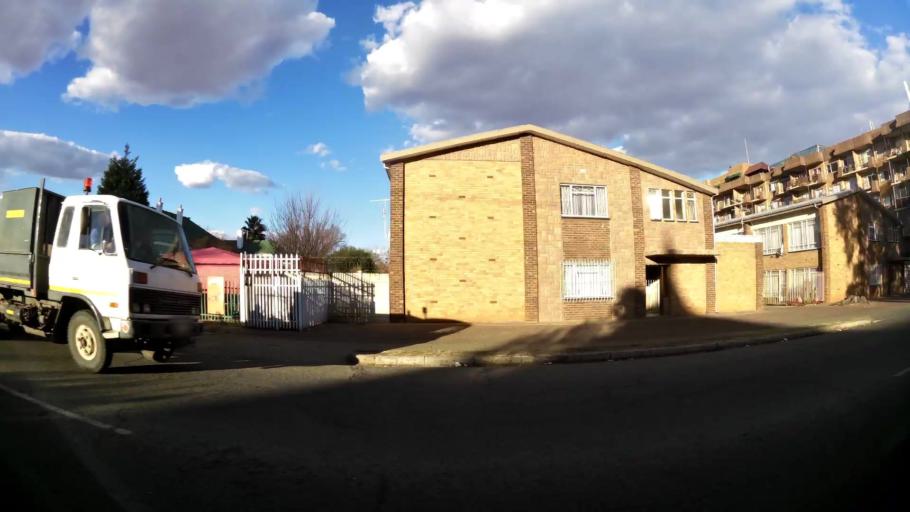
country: ZA
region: North-West
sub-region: Dr Kenneth Kaunda District Municipality
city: Potchefstroom
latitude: -26.7192
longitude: 27.0966
